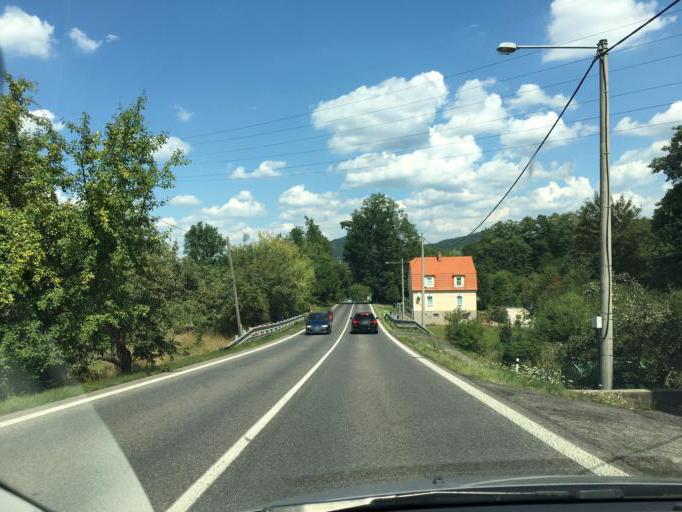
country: CZ
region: Ustecky
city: Ceska Kamenice
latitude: 50.7939
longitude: 14.3984
